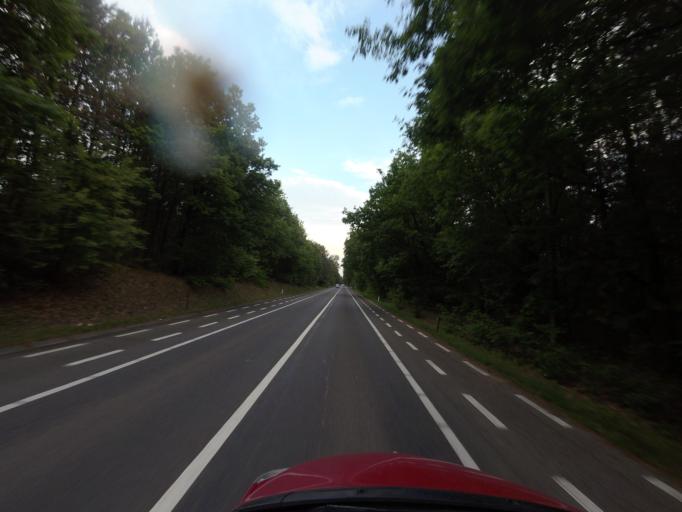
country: BE
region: Flanders
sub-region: Provincie Limburg
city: Overpelt
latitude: 51.1605
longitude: 5.3646
